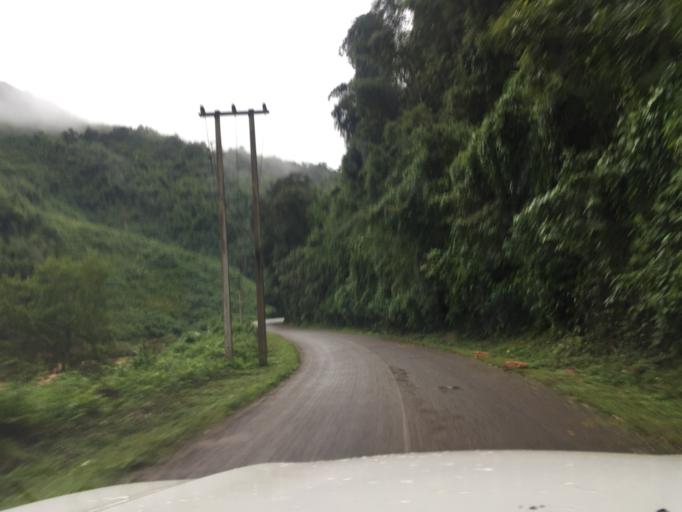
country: LA
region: Oudomxai
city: Muang La
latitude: 20.9209
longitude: 102.2016
